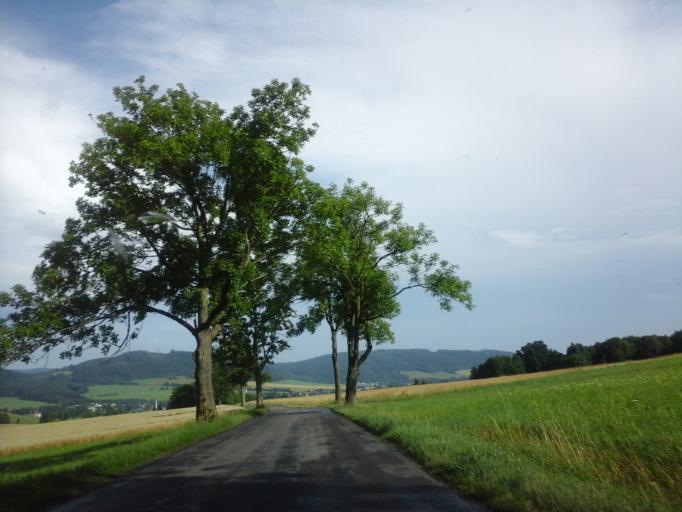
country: CZ
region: Pardubicky
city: Cervena Voda
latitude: 50.0527
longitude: 16.7207
